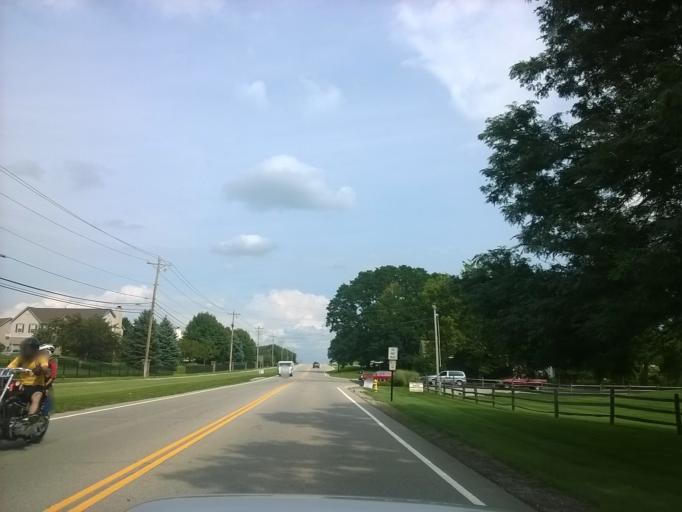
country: US
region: Indiana
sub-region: Hamilton County
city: Carmel
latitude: 39.9785
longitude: -86.0787
